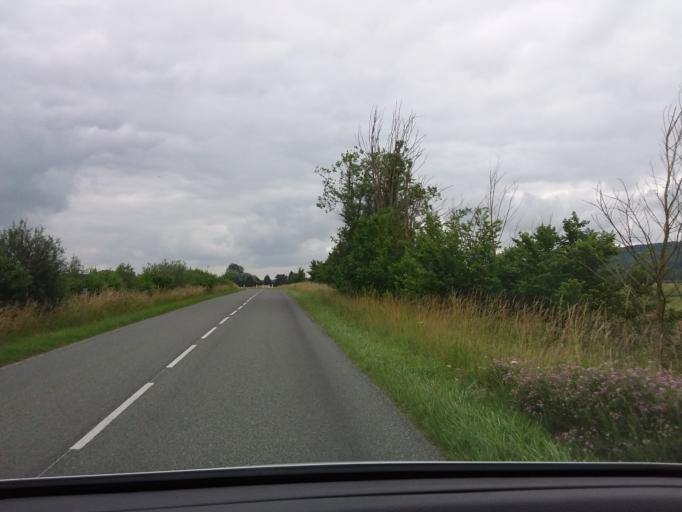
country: FR
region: Picardie
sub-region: Departement de l'Aisne
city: Vailly-sur-Aisne
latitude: 49.4007
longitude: 3.5901
